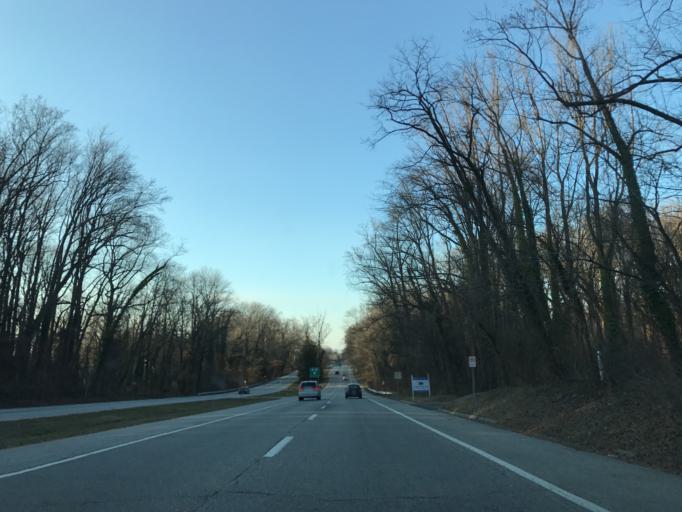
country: US
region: Maryland
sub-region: Anne Arundel County
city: Naval Academy
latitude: 39.0034
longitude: -76.4829
